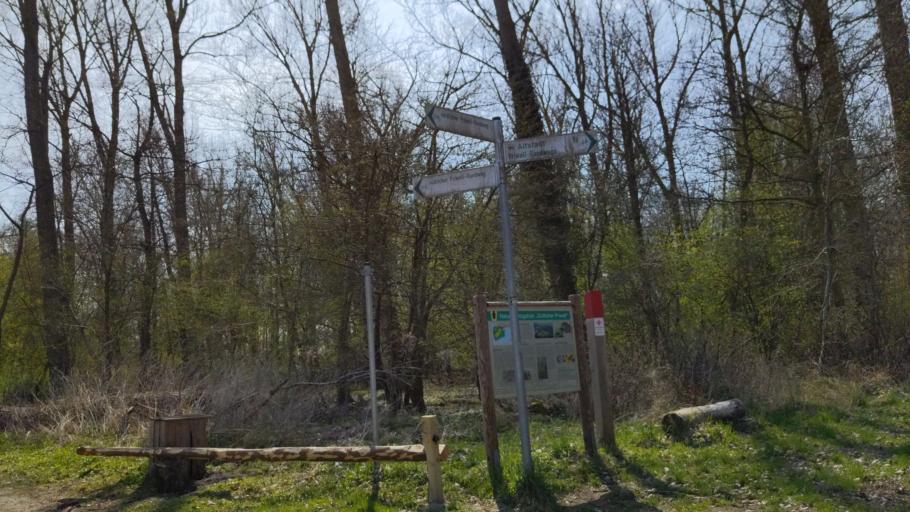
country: DE
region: Schleswig-Holstein
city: Travemuende
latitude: 53.9520
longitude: 10.8763
